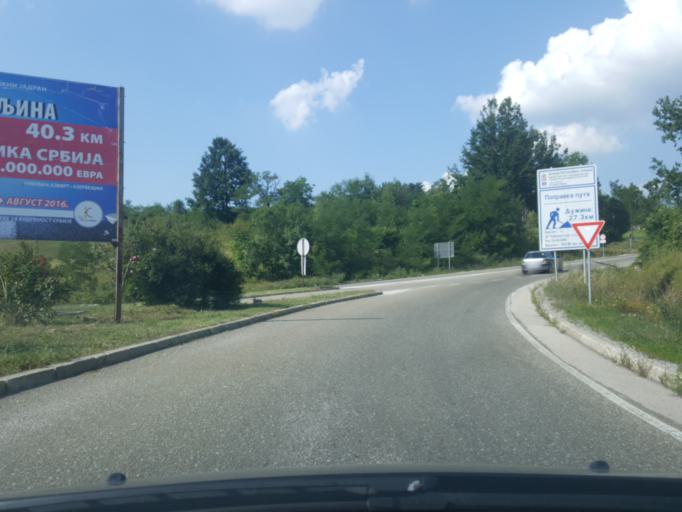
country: RS
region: Central Serbia
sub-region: Moravicki Okrug
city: Gornji Milanovac
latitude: 44.1211
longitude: 20.4835
